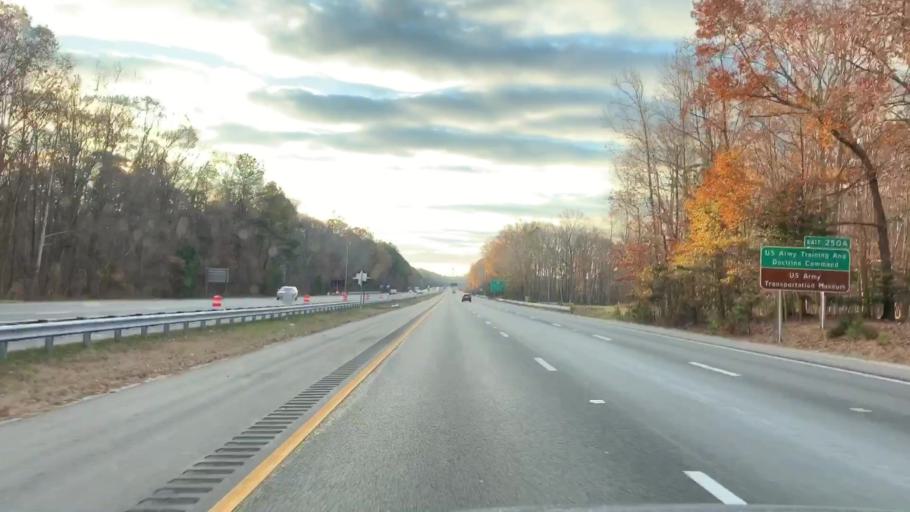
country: US
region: Virginia
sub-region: York County
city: Yorktown
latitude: 37.1925
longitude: -76.5634
